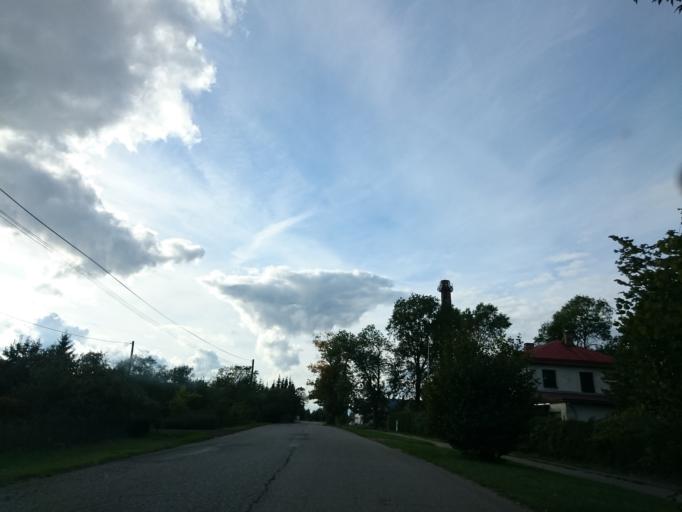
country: LV
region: Adazi
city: Adazi
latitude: 57.0683
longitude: 24.3571
